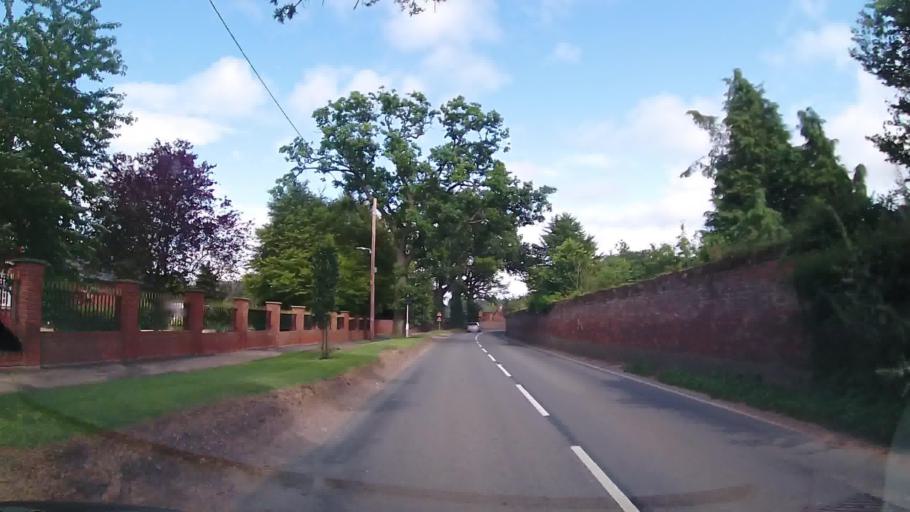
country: GB
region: England
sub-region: Shropshire
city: Great Ness
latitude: 52.7949
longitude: -2.9066
